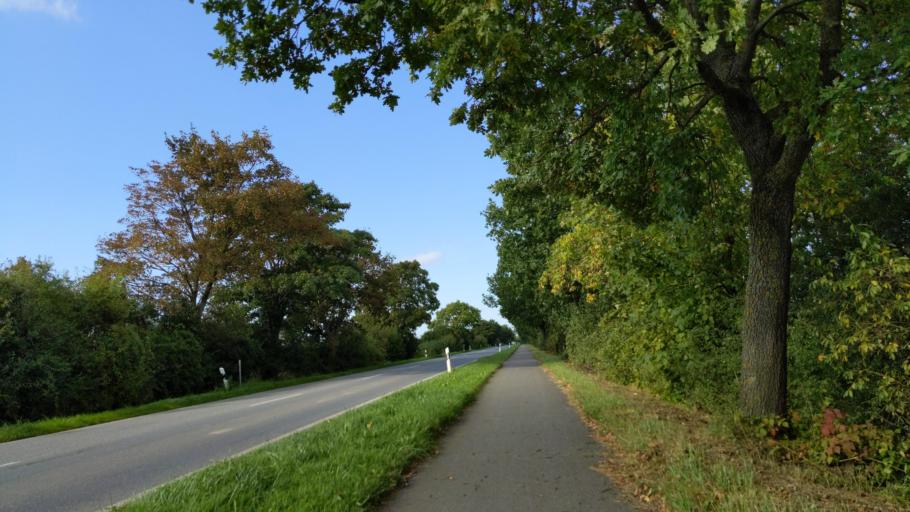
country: DE
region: Schleswig-Holstein
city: Stockelsdorf
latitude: 53.9387
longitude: 10.6312
